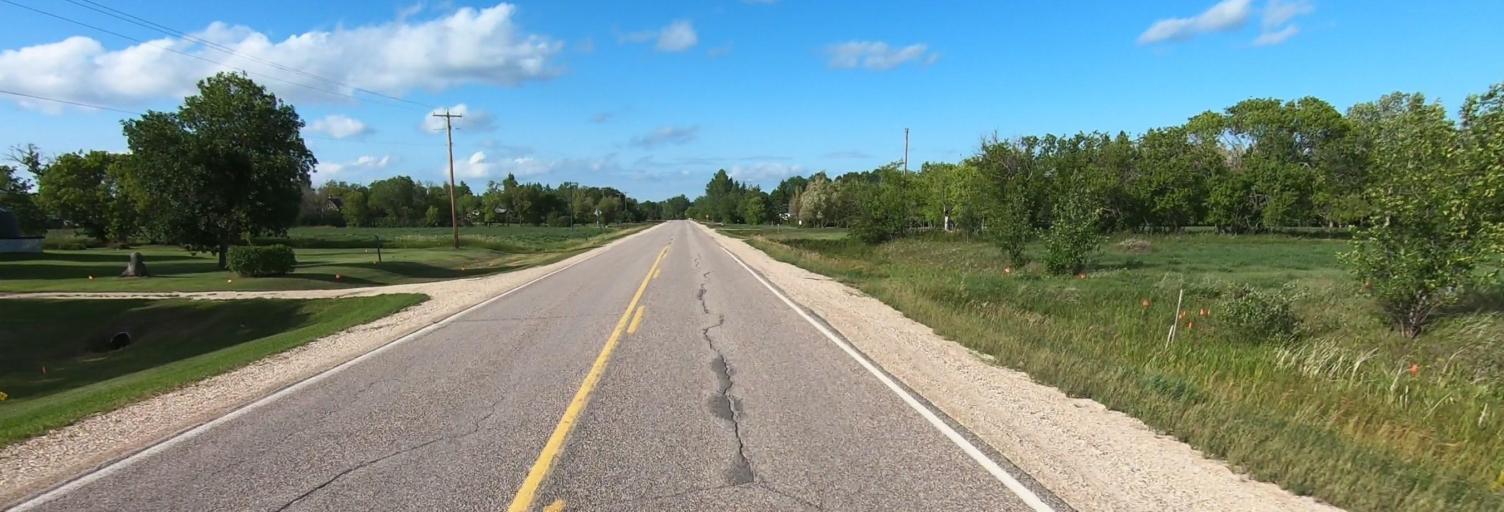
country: CA
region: Manitoba
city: Selkirk
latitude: 50.2141
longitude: -96.8409
